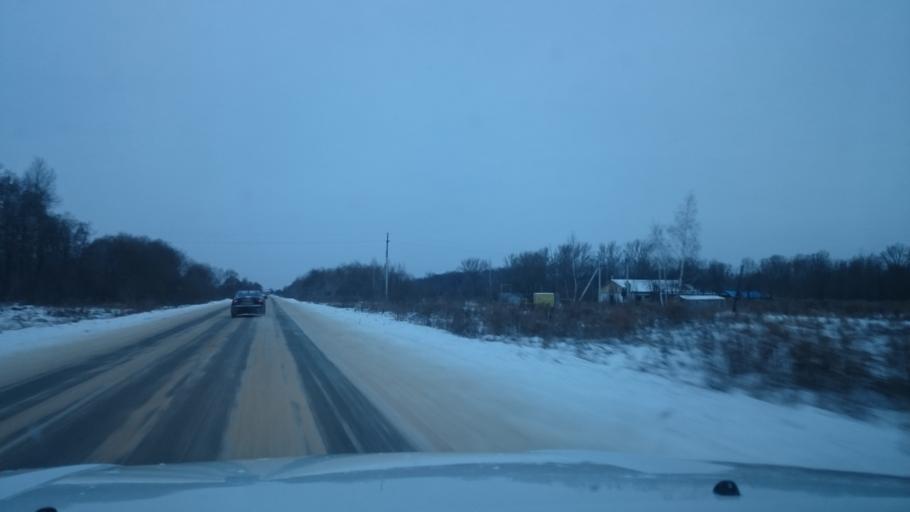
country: RU
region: Tula
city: Leninskiy
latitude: 54.2479
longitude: 37.3894
